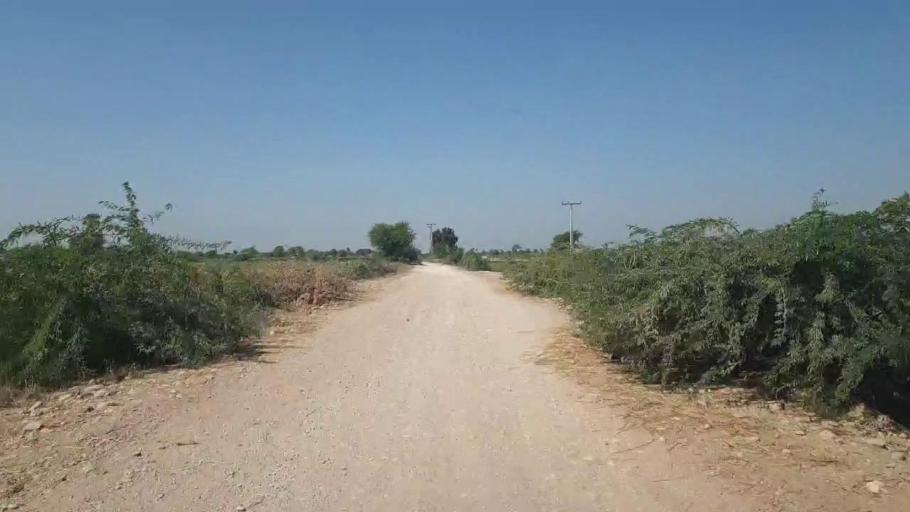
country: PK
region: Sindh
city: Talhar
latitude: 24.8343
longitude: 68.8017
